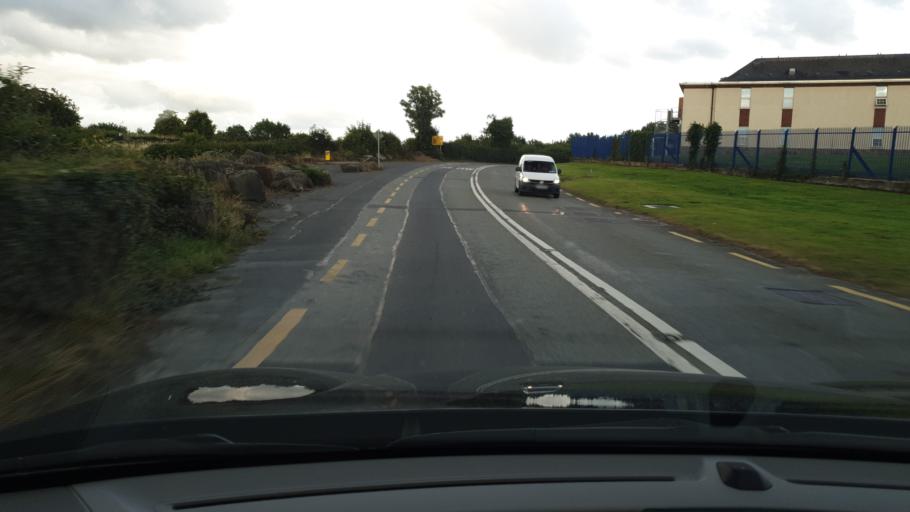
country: IE
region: Leinster
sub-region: South Dublin
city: Saggart
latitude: 53.3104
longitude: -6.4433
